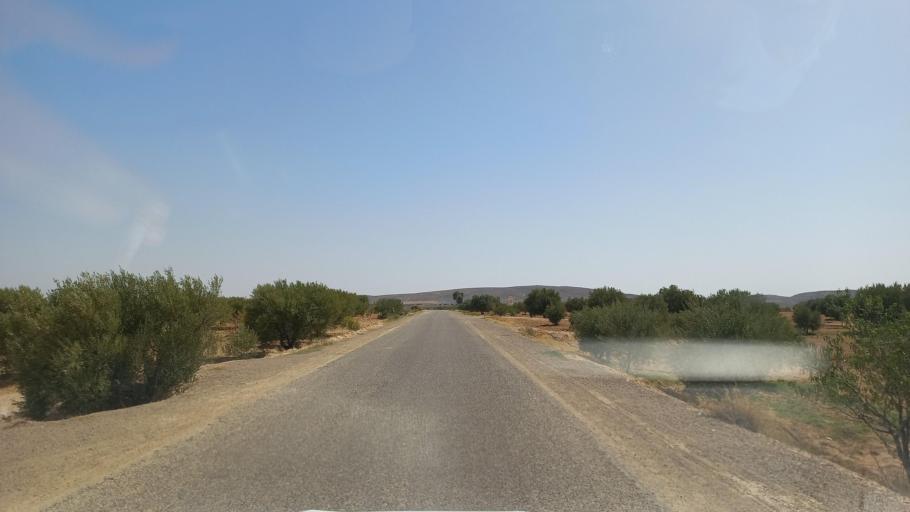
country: TN
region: Al Qasrayn
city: Kasserine
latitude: 35.2135
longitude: 9.0422
